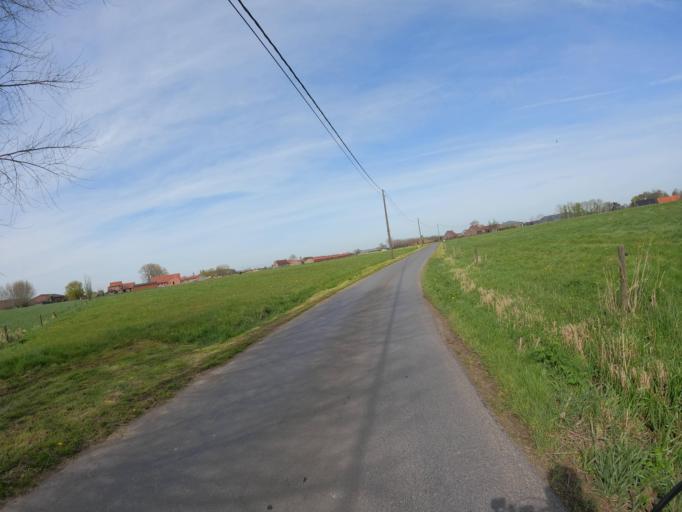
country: BE
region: Flanders
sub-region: Provincie West-Vlaanderen
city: Ruiselede
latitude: 51.0262
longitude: 3.3654
